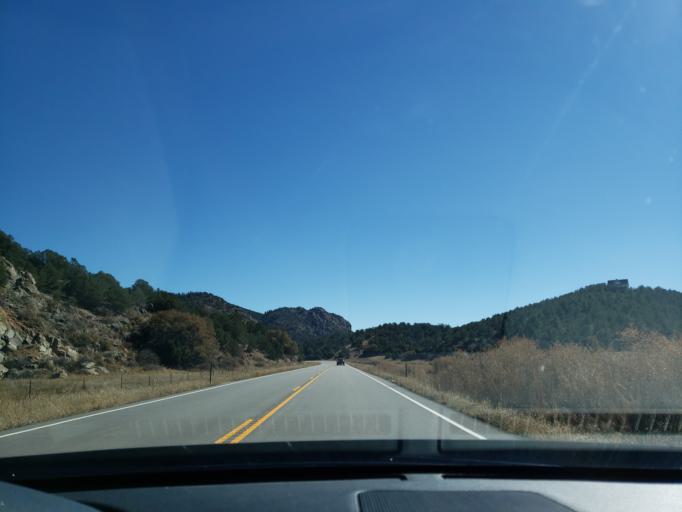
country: US
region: Colorado
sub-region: Fremont County
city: Canon City
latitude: 38.6201
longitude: -105.4513
